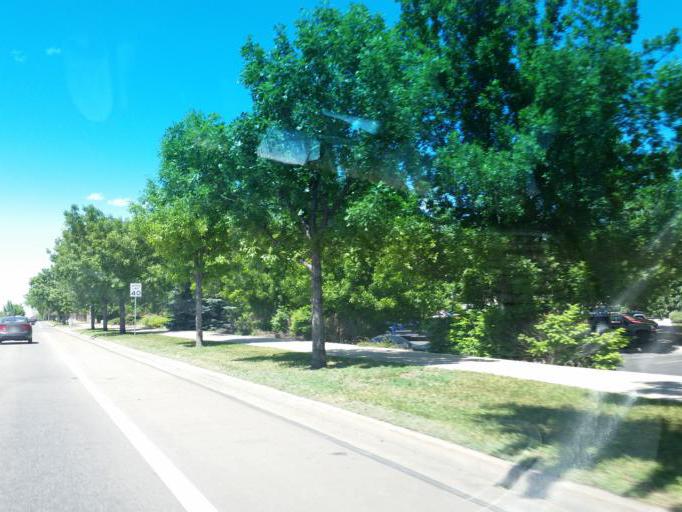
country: US
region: Colorado
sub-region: Larimer County
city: Fort Collins
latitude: 40.5243
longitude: -105.0961
